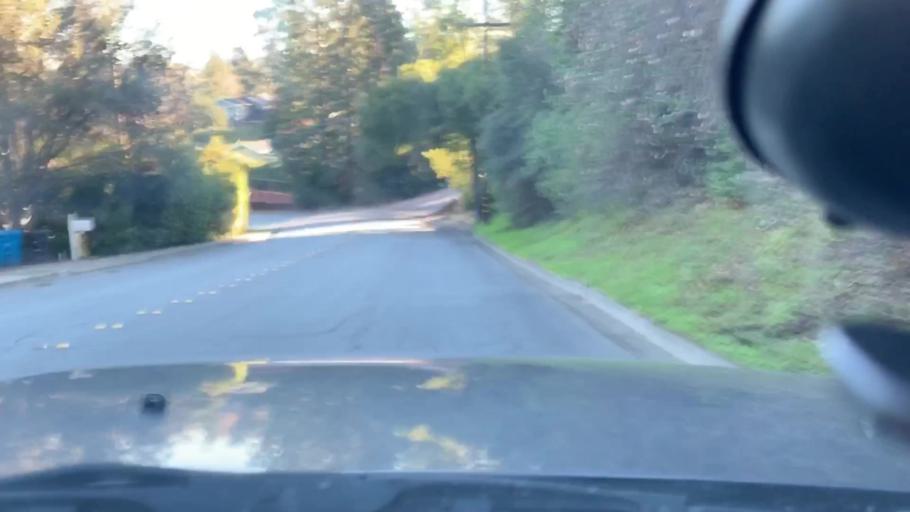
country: US
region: California
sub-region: San Mateo County
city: Ladera
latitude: 37.3999
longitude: -122.2029
